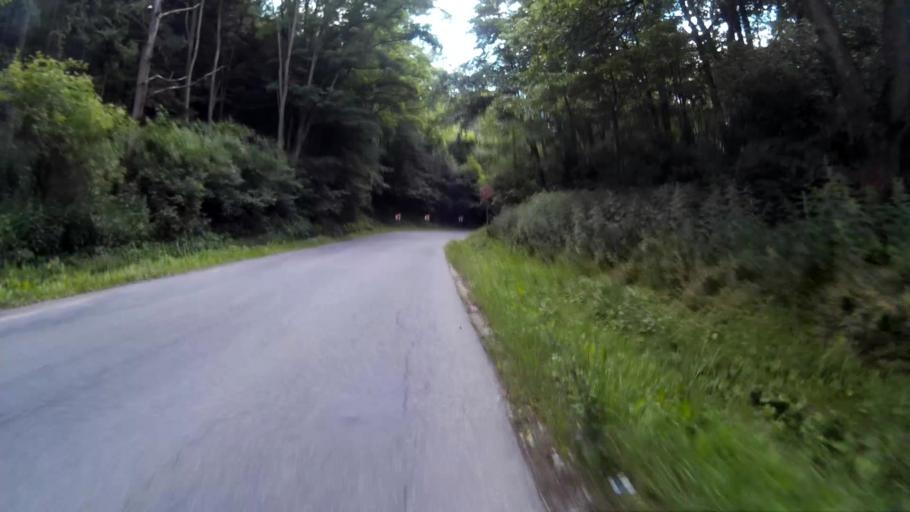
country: CZ
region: South Moravian
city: Strelice
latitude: 49.1512
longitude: 16.4690
